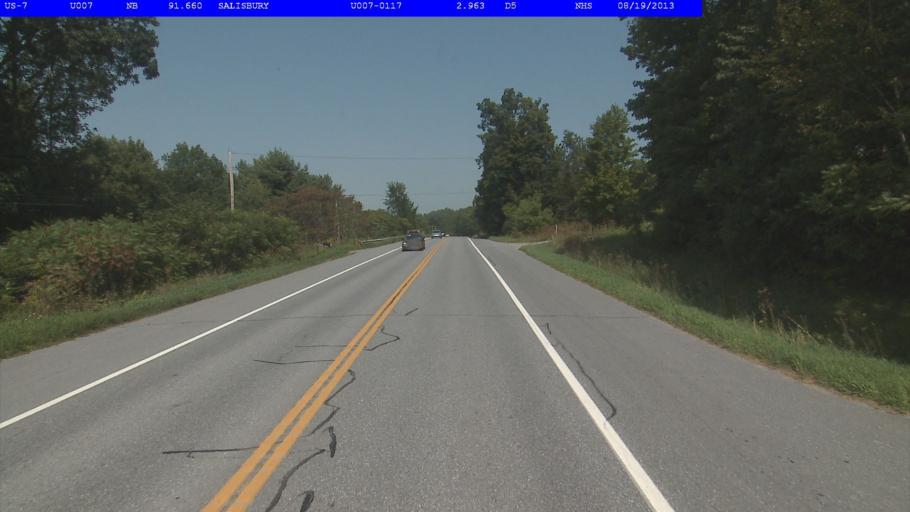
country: US
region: Vermont
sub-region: Addison County
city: Middlebury (village)
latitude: 43.9344
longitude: -73.1091
